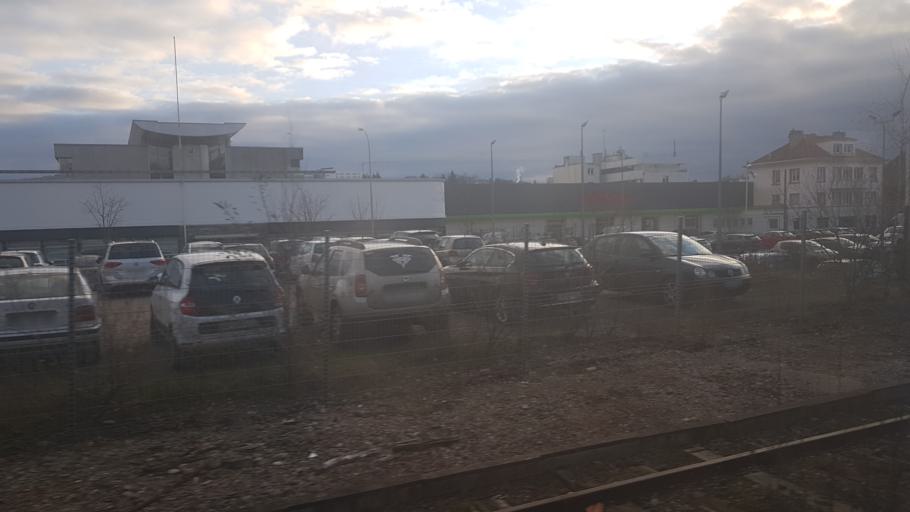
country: FR
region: Lorraine
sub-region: Departement des Vosges
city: Epinal
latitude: 48.1801
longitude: 6.4407
